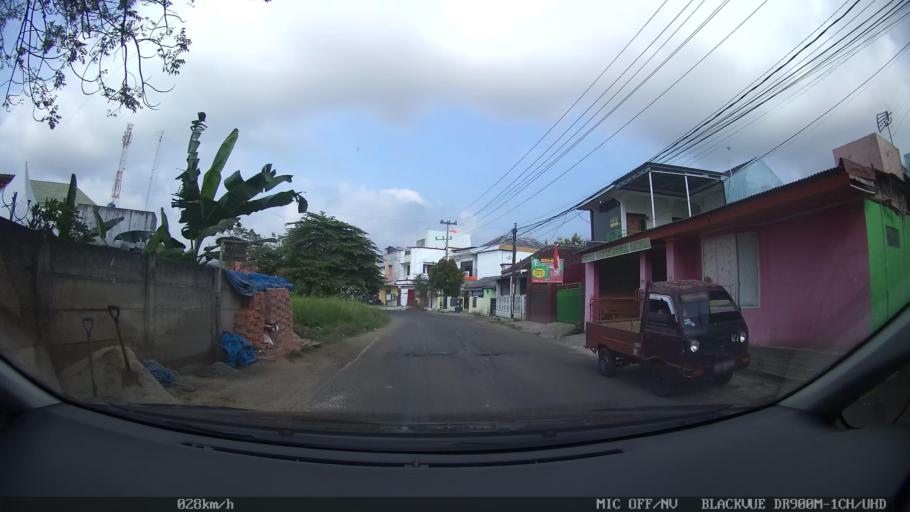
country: ID
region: Lampung
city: Bandarlampung
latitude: -5.4376
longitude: 105.2539
